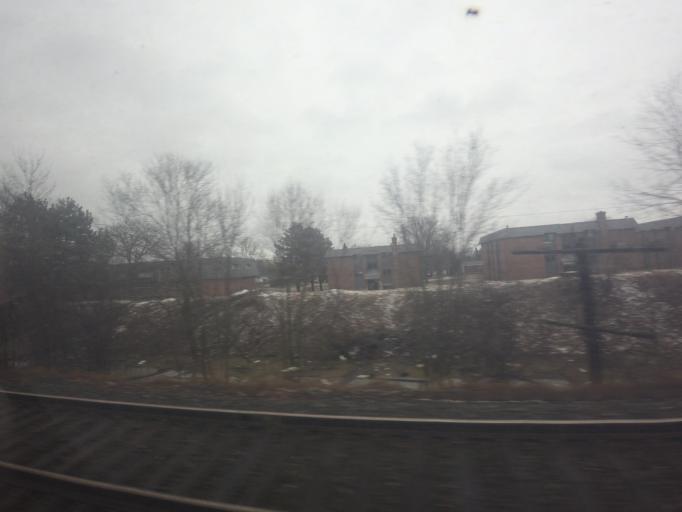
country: CA
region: Ontario
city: Kingston
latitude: 44.2275
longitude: -76.6447
